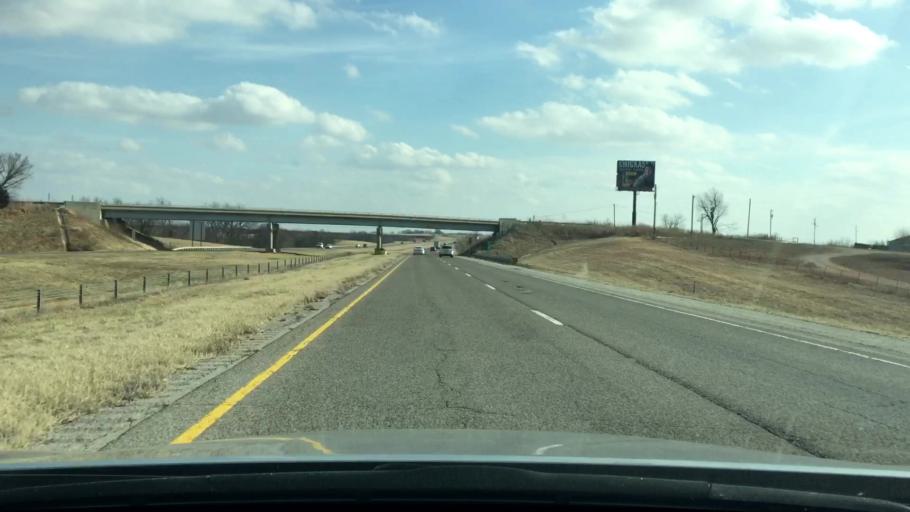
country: US
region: Oklahoma
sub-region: Garvin County
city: Maysville
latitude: 34.8974
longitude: -97.3457
